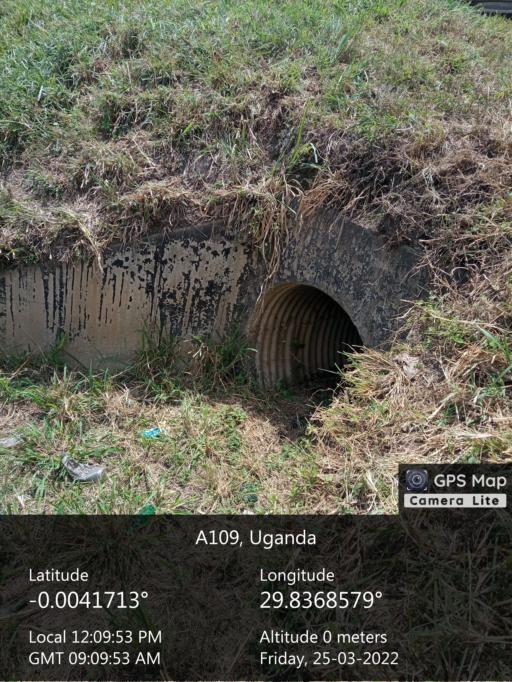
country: UG
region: Western Region
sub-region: Kasese District
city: Kilembe
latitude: -0.0035
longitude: 29.8388
